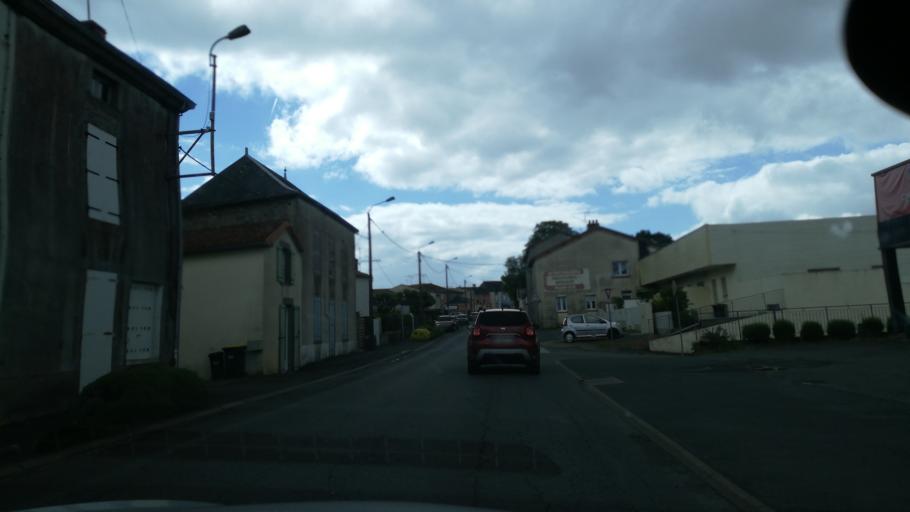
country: FR
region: Poitou-Charentes
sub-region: Departement des Deux-Sevres
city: Moncoutant
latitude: 46.7264
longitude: -0.5902
